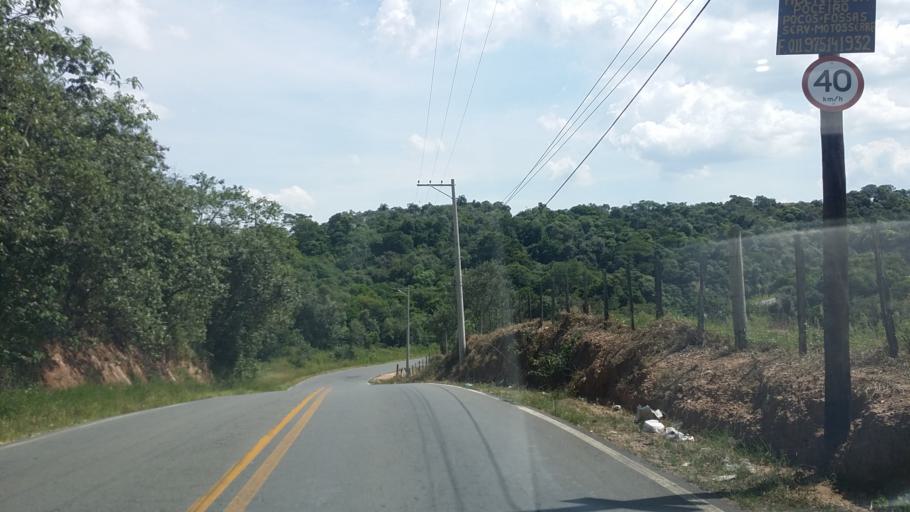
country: BR
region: Sao Paulo
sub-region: Itupeva
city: Itupeva
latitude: -23.1858
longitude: -47.0679
